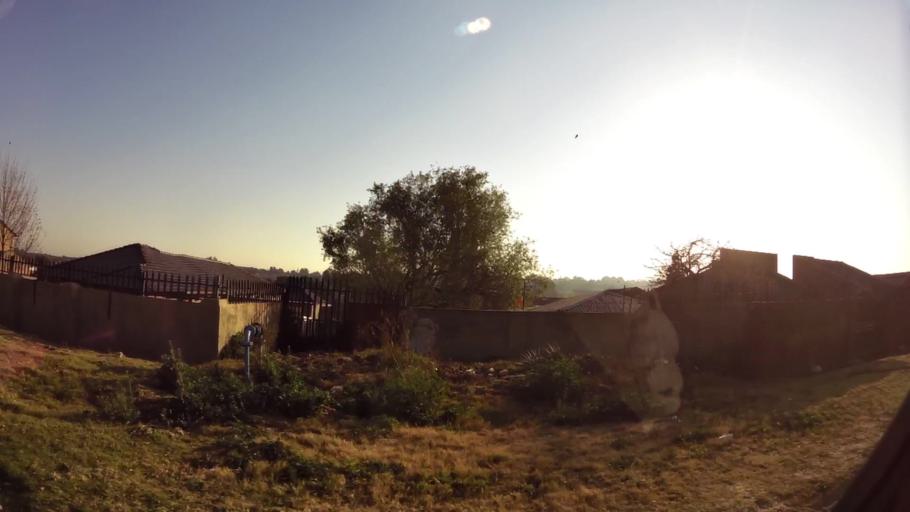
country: ZA
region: Gauteng
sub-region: City of Johannesburg Metropolitan Municipality
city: Soweto
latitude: -26.2764
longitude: 27.9584
